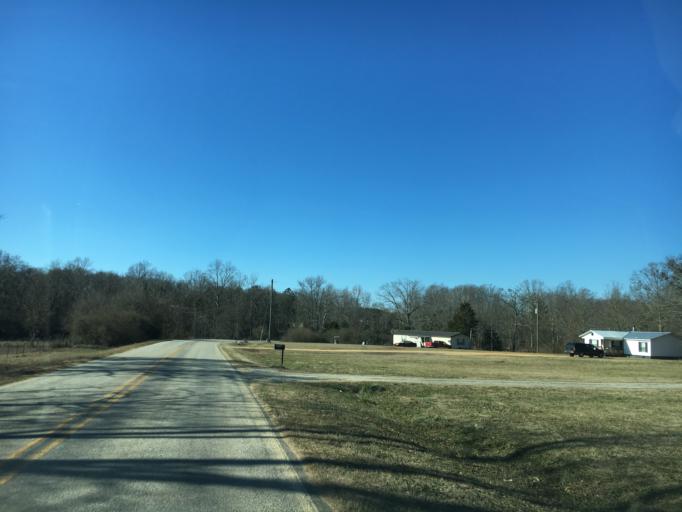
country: US
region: Georgia
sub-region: Hart County
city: Hartwell
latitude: 34.3055
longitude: -82.9920
